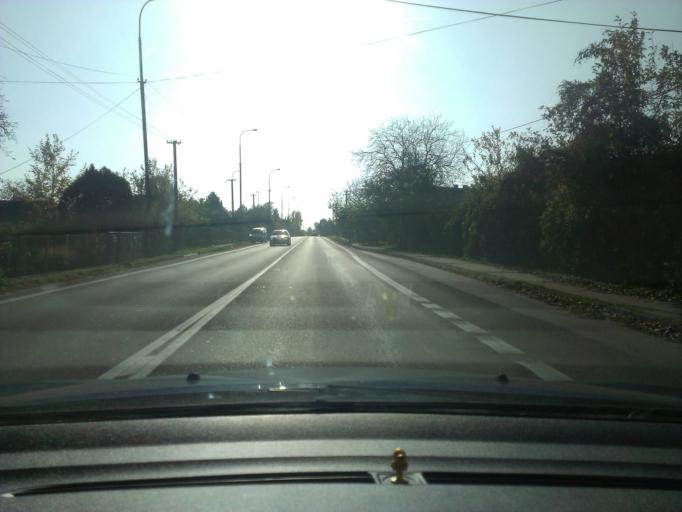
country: SK
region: Nitriansky
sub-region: Okres Komarno
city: Hurbanovo
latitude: 47.8526
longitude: 18.1720
